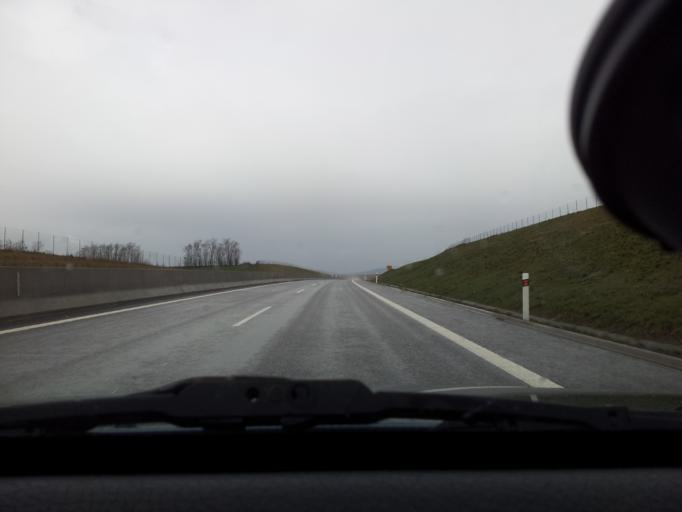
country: SK
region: Nitriansky
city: Zlate Moravce
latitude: 48.3417
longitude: 18.4031
